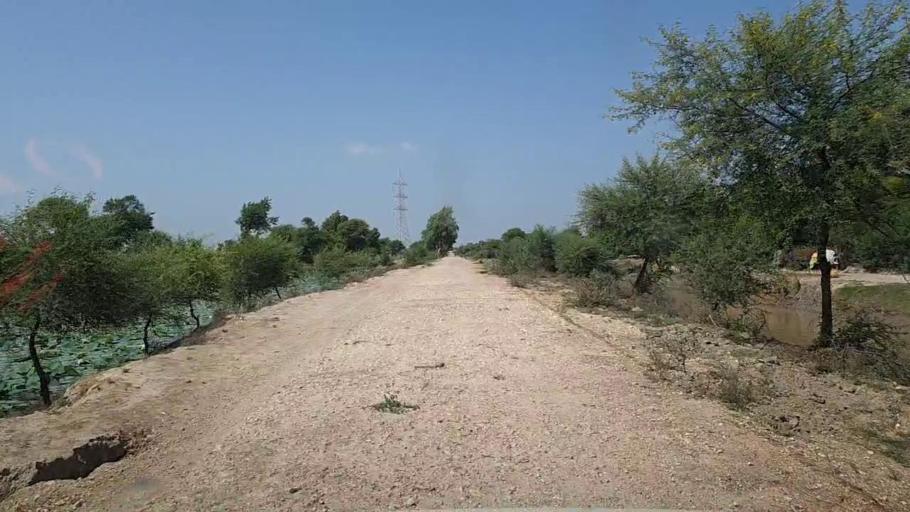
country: PK
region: Sindh
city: Kario
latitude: 24.6564
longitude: 68.5511
